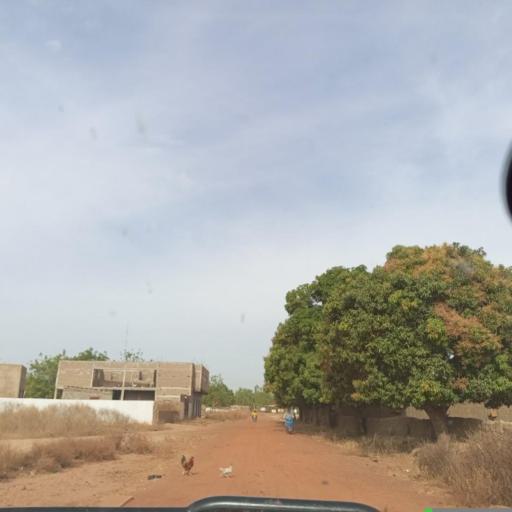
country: ML
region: Koulikoro
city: Koulikoro
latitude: 13.1107
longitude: -7.6515
